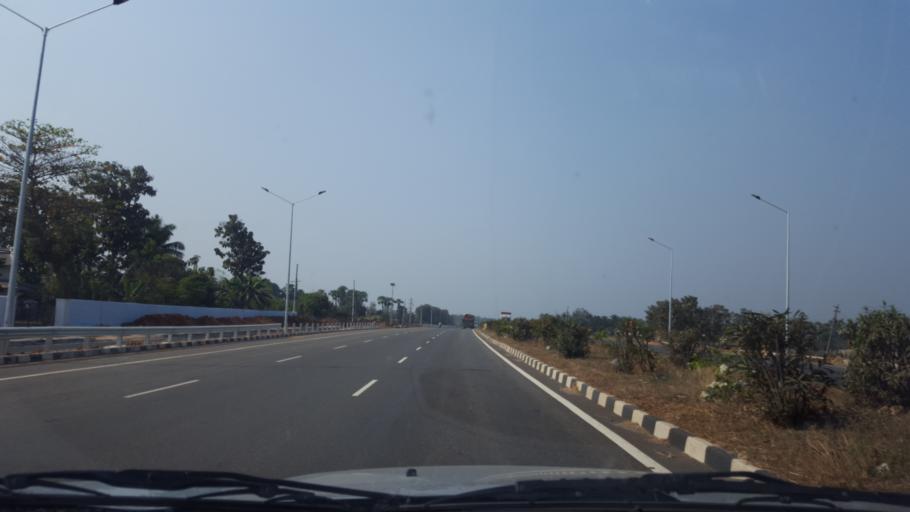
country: IN
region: Andhra Pradesh
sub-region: Vishakhapatnam
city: Bhimunipatnam
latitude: 17.9946
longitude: 83.4716
